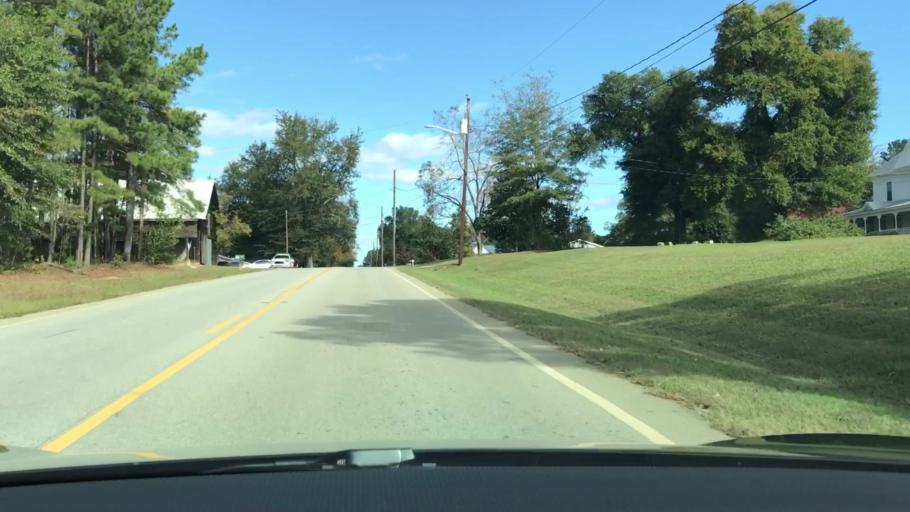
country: US
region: Georgia
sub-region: Jefferson County
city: Wrens
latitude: 33.2082
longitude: -82.4688
